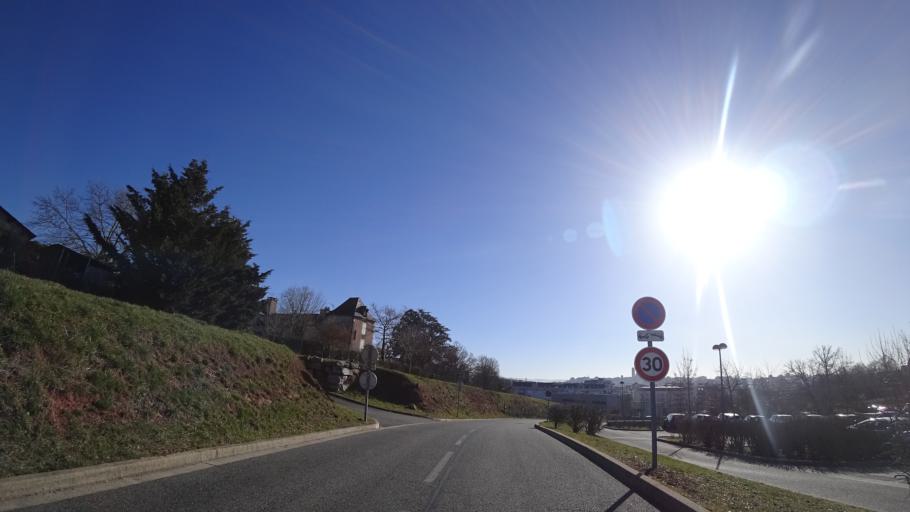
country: FR
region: Midi-Pyrenees
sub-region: Departement de l'Aveyron
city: Olemps
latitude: 44.3609
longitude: 2.5523
